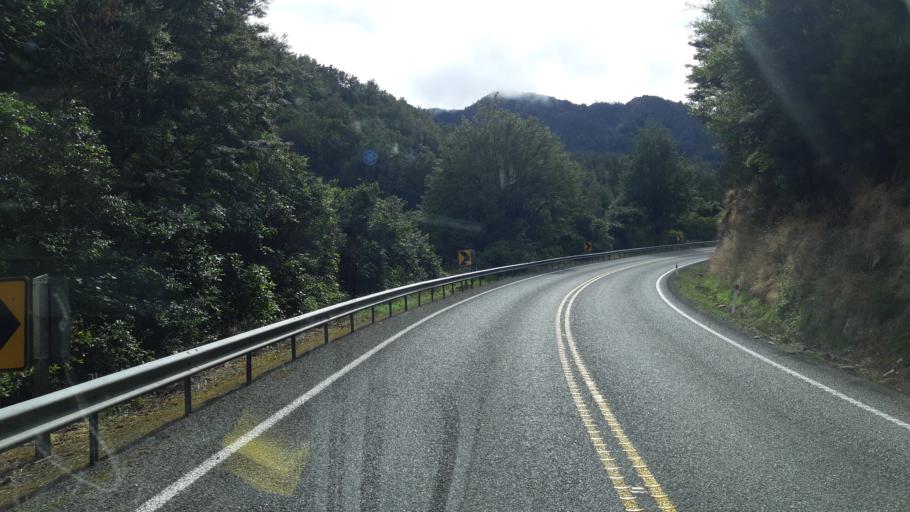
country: NZ
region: West Coast
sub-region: Buller District
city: Westport
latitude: -41.7696
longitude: 172.2304
